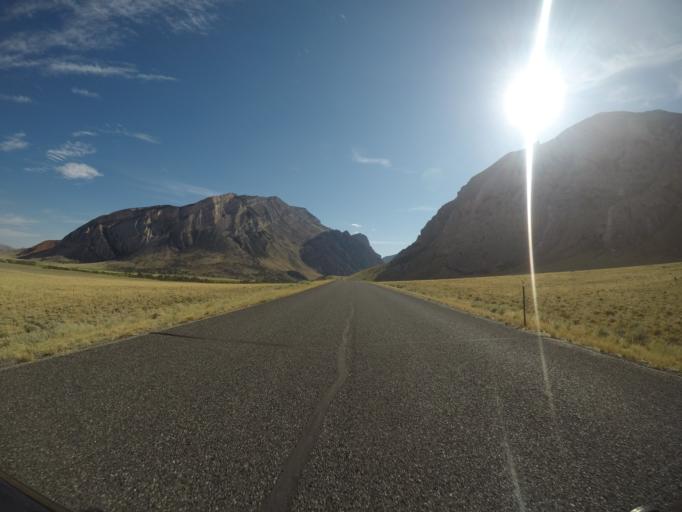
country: US
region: Montana
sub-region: Carbon County
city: Red Lodge
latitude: 44.8601
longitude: -109.2901
